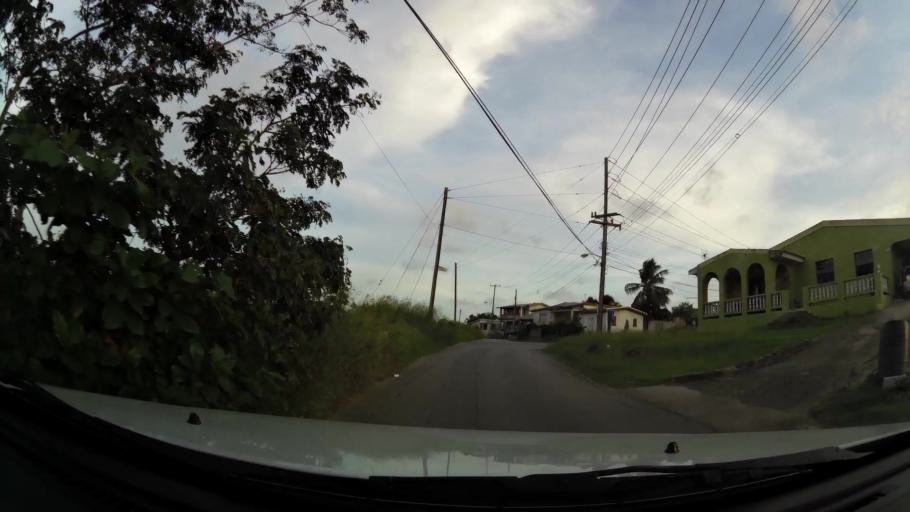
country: BB
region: Saint Philip
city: Crane
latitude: 13.0966
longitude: -59.4920
